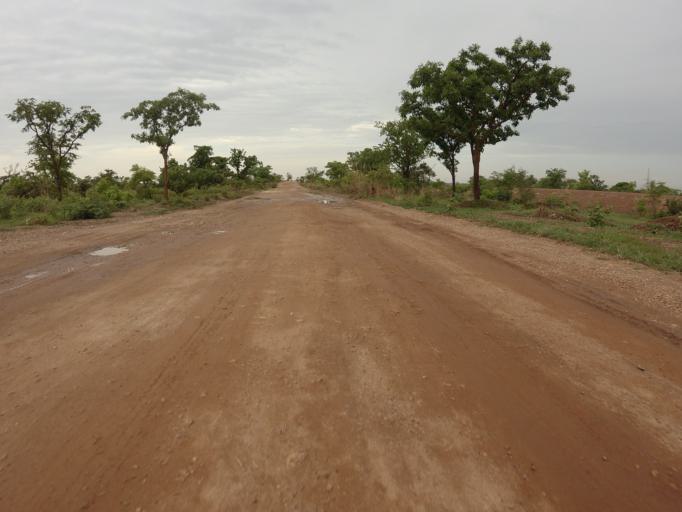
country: GH
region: Upper East
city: Bolgatanga
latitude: 10.8783
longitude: -0.6269
